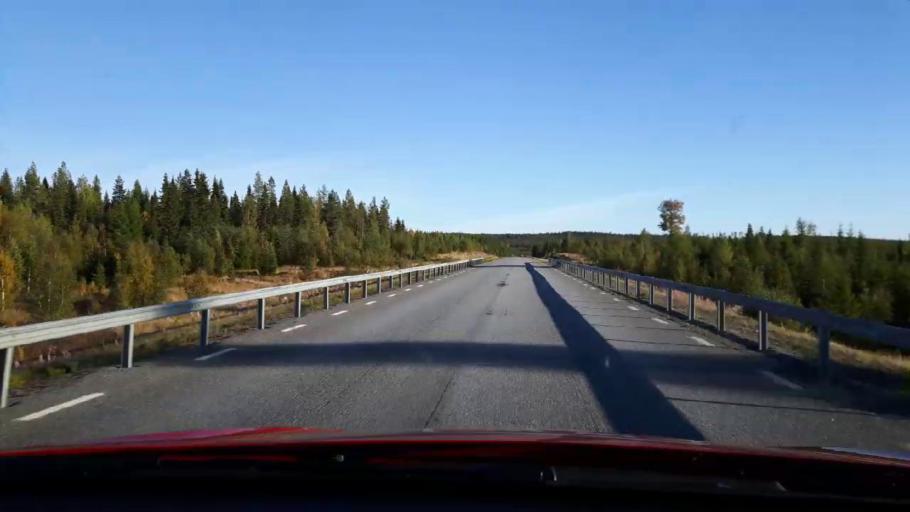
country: SE
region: Jaemtland
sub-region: OEstersunds Kommun
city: Lit
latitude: 63.7735
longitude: 14.7146
